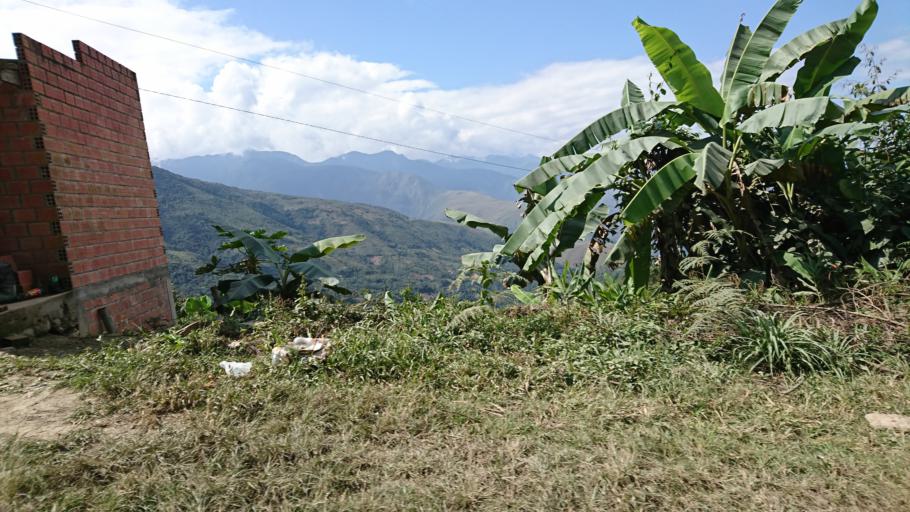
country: BO
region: La Paz
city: Coroico
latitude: -16.1339
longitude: -67.7512
